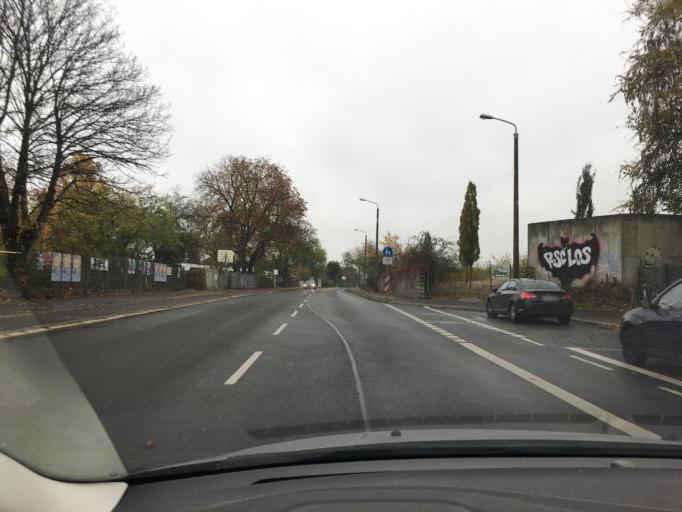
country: DE
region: Saxony
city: Leipzig
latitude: 51.3324
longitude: 12.4230
